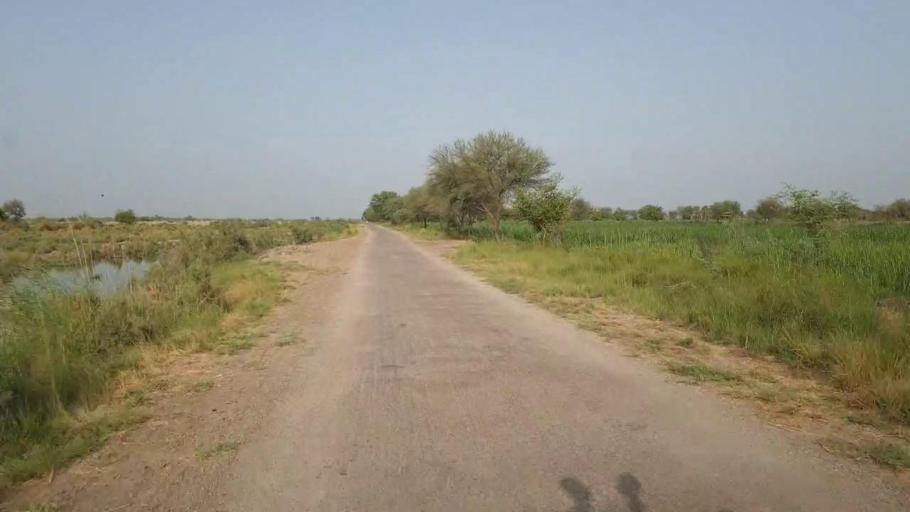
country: PK
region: Sindh
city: Daur
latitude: 26.3403
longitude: 68.2206
